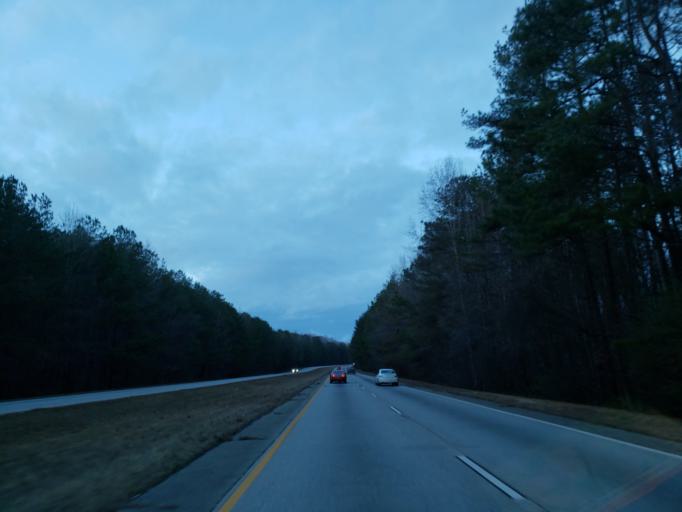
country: US
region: Georgia
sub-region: Fulton County
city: Union City
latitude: 33.6907
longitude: -84.5744
